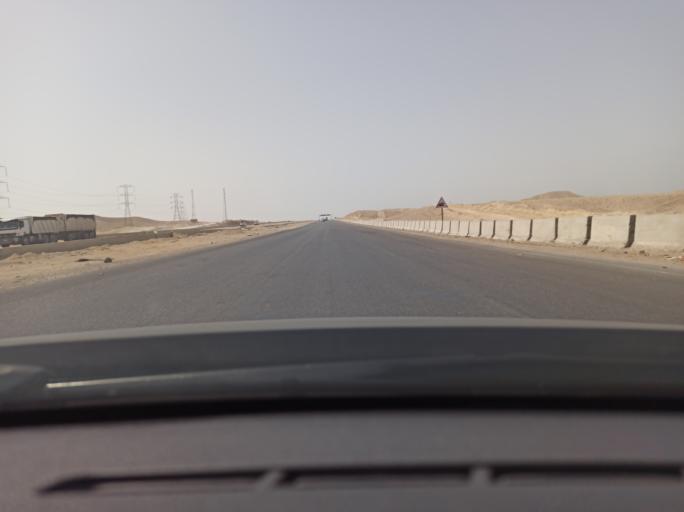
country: EG
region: Al Jizah
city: As Saff
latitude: 29.5457
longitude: 31.3932
